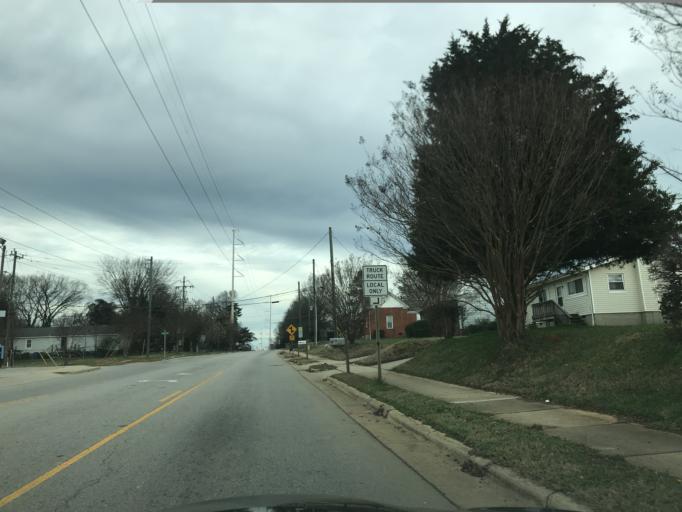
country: US
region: North Carolina
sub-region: Wake County
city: Raleigh
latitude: 35.7628
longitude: -78.6314
